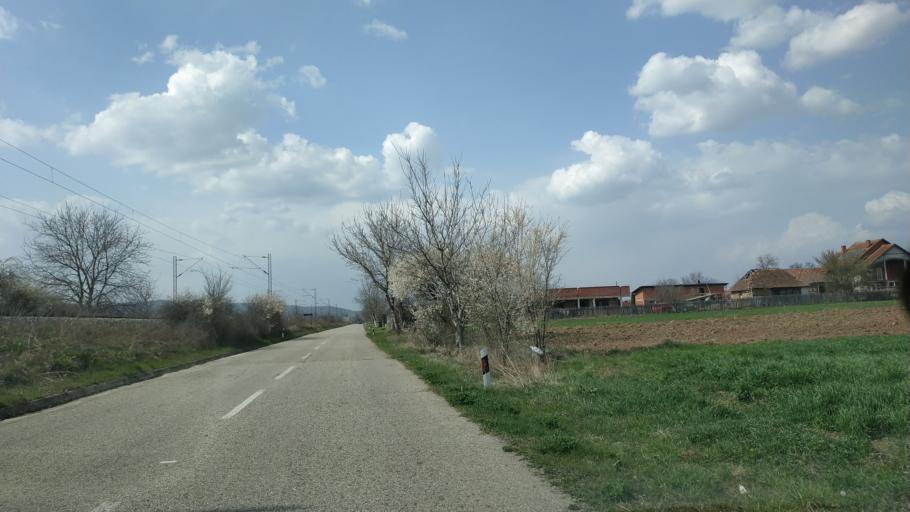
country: RS
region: Central Serbia
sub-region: Nisavski Okrug
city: Razanj
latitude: 43.5695
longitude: 21.5882
